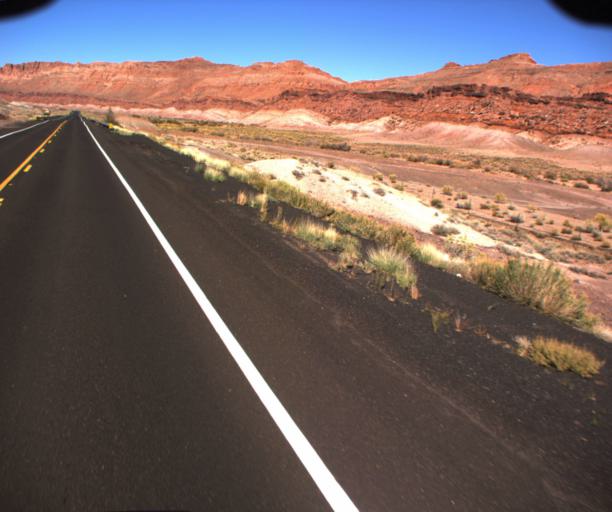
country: US
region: Arizona
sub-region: Coconino County
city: Tuba City
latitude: 36.1963
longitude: -111.3932
